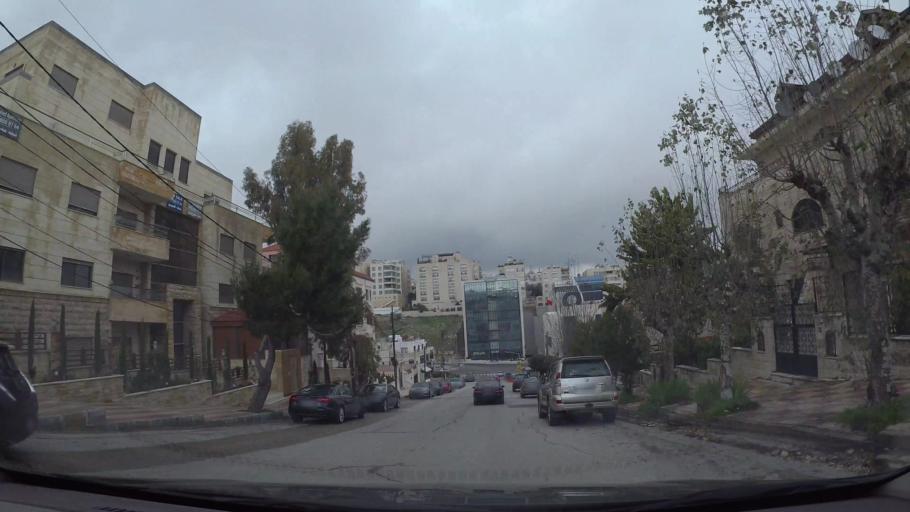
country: JO
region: Amman
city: Amman
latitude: 31.9539
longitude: 35.8841
